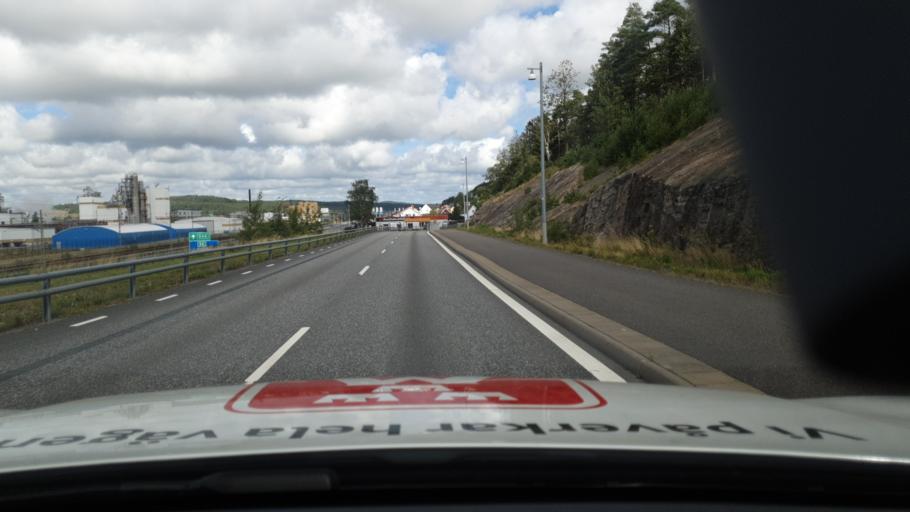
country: SE
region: Vaestra Goetaland
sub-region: Ale Kommun
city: Surte
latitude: 57.8439
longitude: 12.0135
